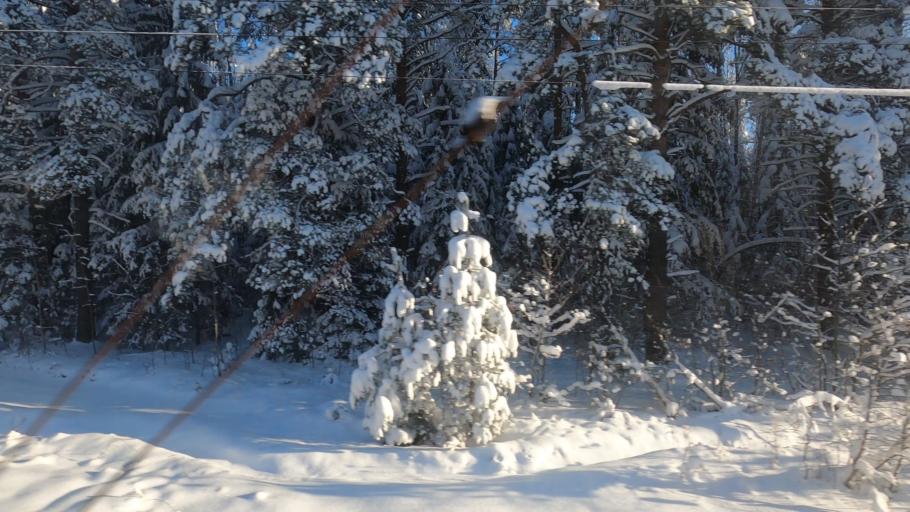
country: RU
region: Moskovskaya
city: Zhukovka
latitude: 56.4877
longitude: 37.5501
